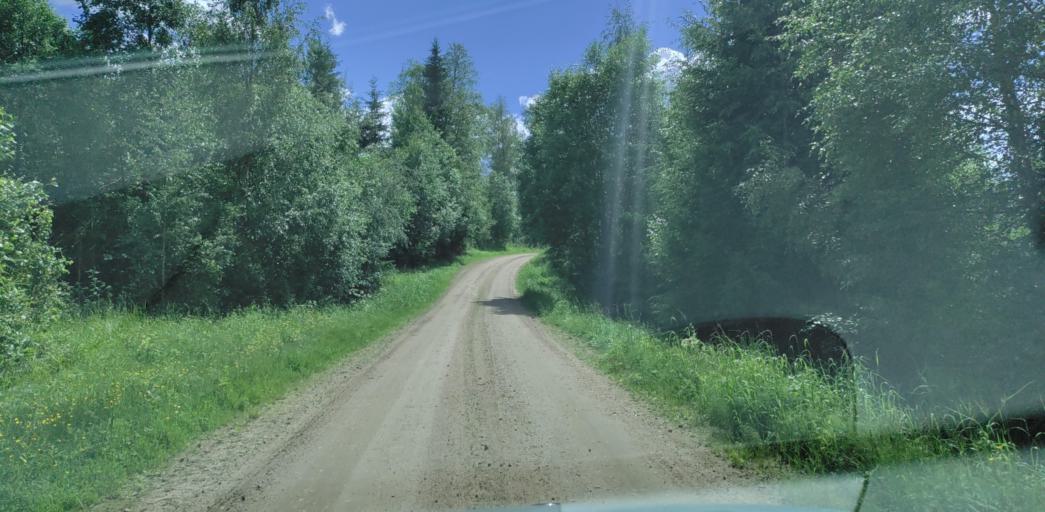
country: SE
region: Vaermland
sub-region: Hagfors Kommun
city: Ekshaerad
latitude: 60.0994
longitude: 13.3175
